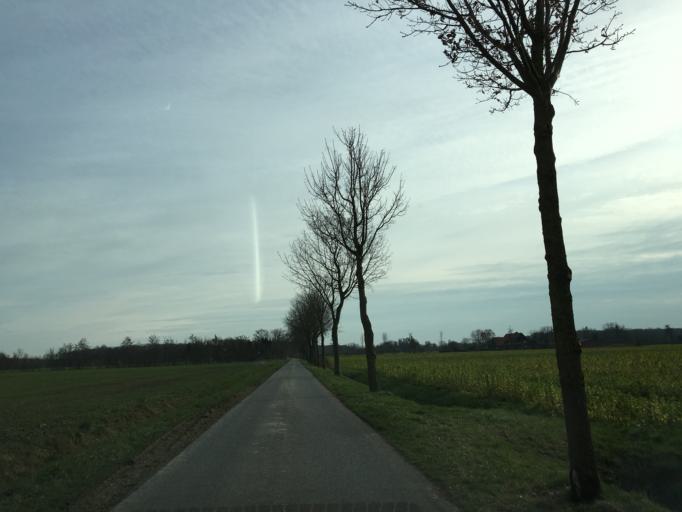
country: DE
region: North Rhine-Westphalia
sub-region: Regierungsbezirk Munster
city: Greven
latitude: 52.0283
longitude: 7.5784
